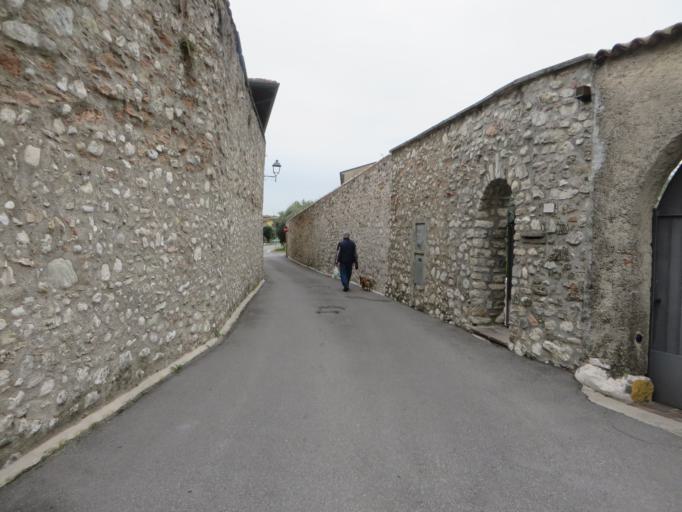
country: IT
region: Lombardy
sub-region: Provincia di Brescia
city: Toscolano Maderno
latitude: 45.6360
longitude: 10.6104
